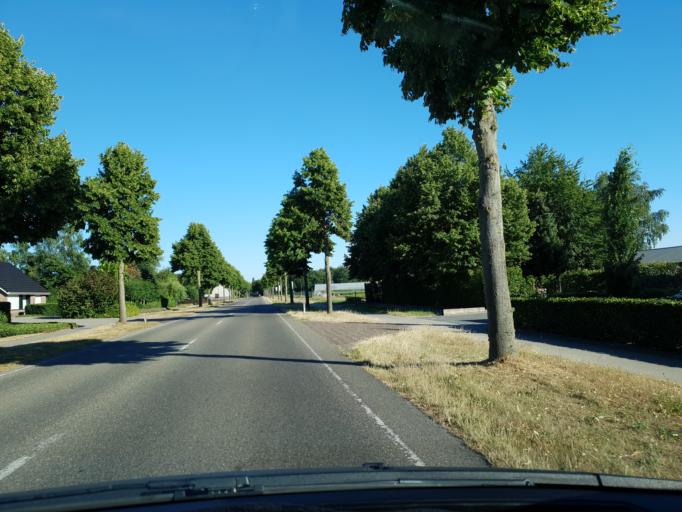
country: NL
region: North Brabant
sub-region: Gemeente Zundert
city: Zundert
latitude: 51.4683
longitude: 4.6848
